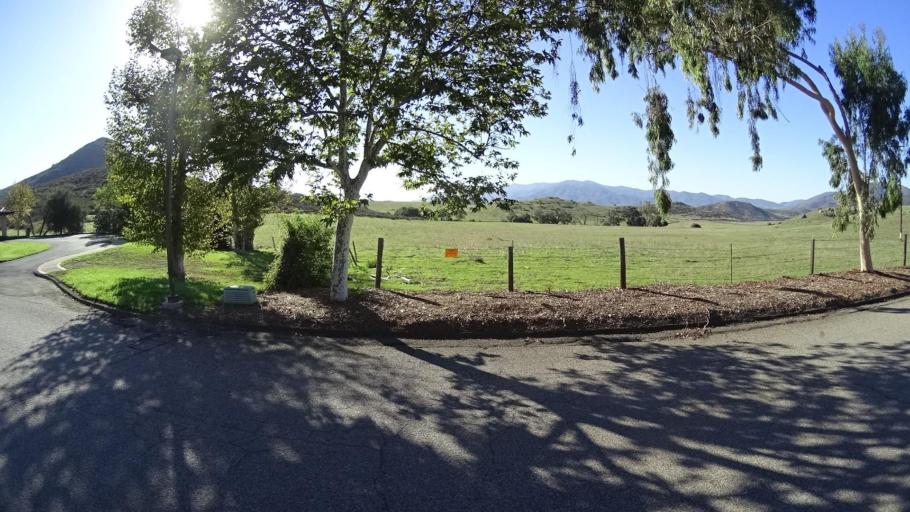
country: US
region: California
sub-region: San Diego County
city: Jamul
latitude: 32.6975
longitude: -116.8538
